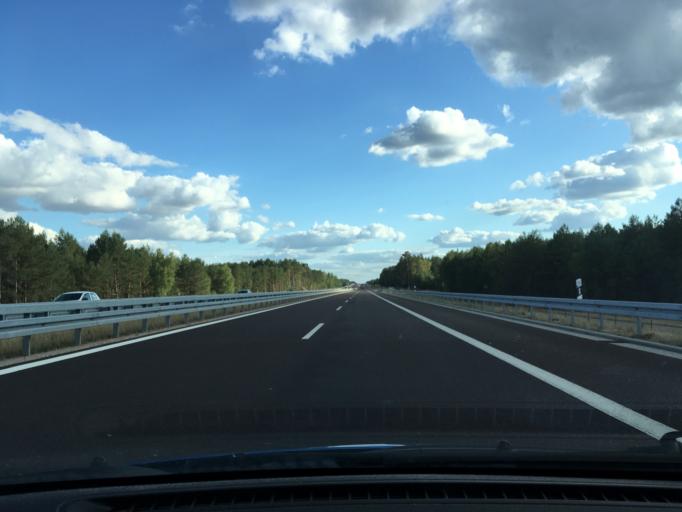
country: DE
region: Mecklenburg-Vorpommern
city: Ludwigslust
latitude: 53.3188
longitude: 11.5279
